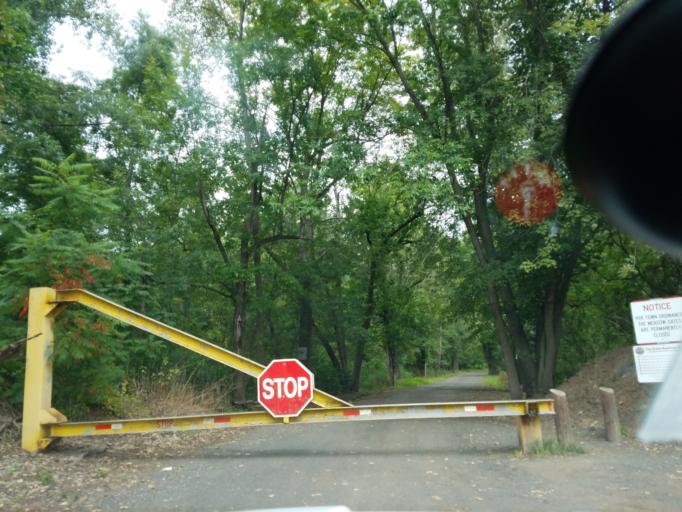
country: US
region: Connecticut
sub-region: Hartford County
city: Glastonbury Center
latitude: 41.6684
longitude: -72.6313
